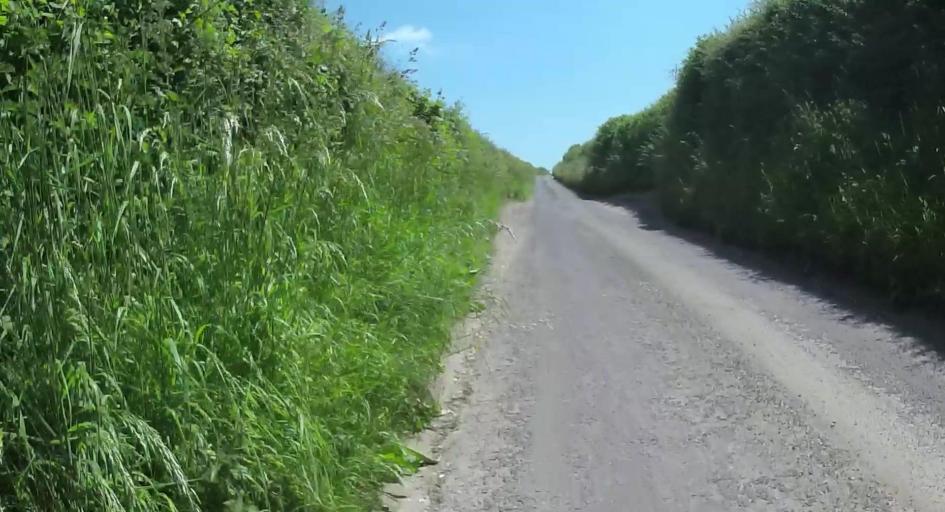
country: GB
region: England
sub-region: Hampshire
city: Kings Worthy
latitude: 51.0804
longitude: -1.2718
